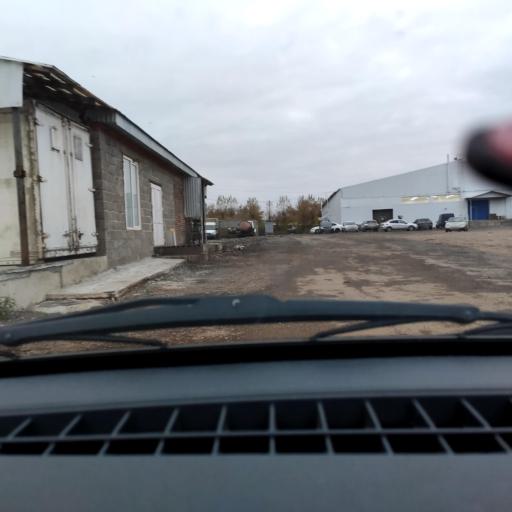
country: RU
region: Bashkortostan
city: Ufa
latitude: 54.7437
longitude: 55.9297
